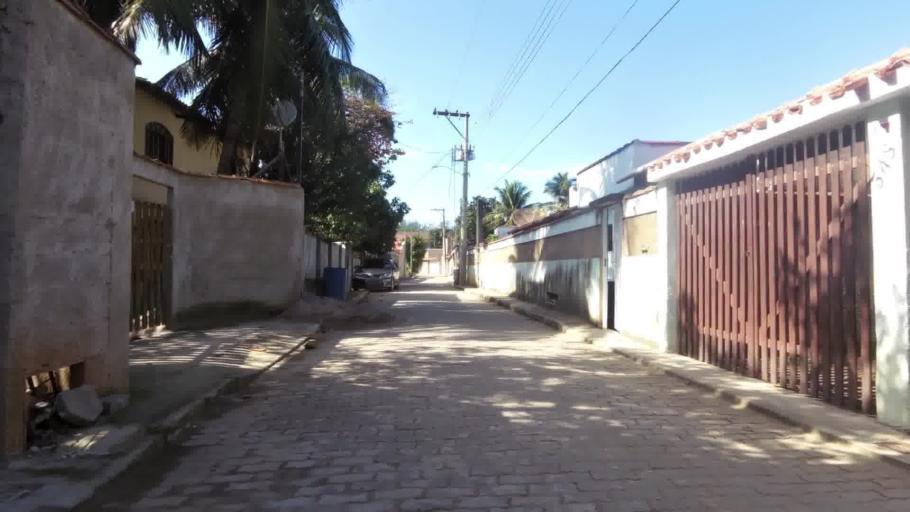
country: BR
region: Espirito Santo
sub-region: Piuma
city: Piuma
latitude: -20.8143
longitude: -40.6323
